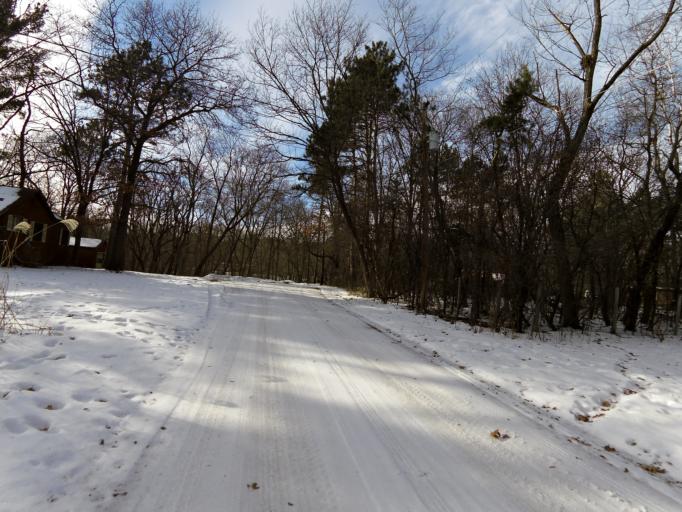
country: US
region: Minnesota
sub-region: Washington County
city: Lake Saint Croix Beach
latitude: 44.9140
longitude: -92.7756
